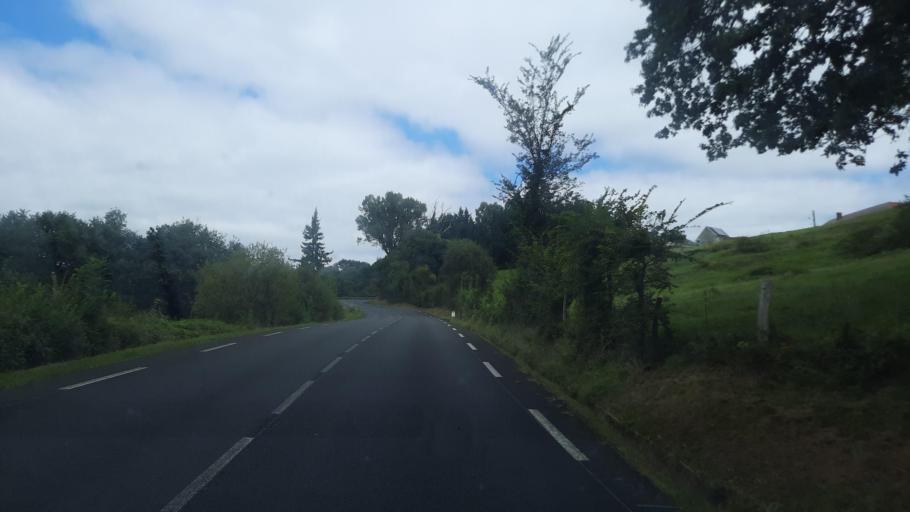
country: FR
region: Midi-Pyrenees
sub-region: Departement des Hautes-Pyrenees
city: Orleix
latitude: 43.2818
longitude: 0.1905
